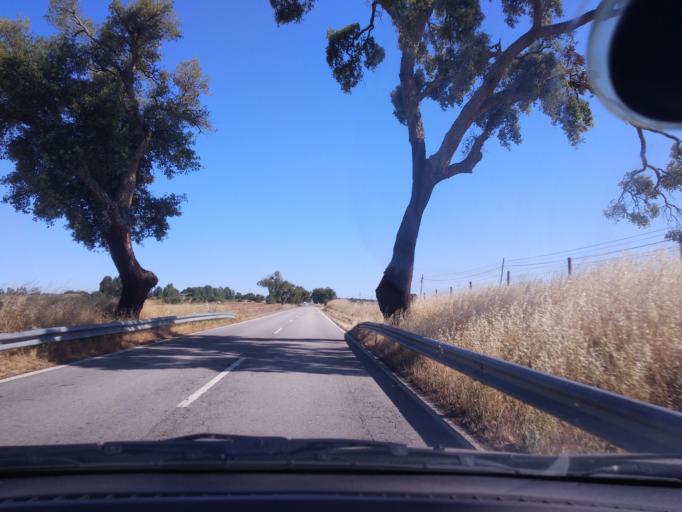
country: PT
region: Portalegre
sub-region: Nisa
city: Nisa
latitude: 39.4357
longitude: -7.6240
